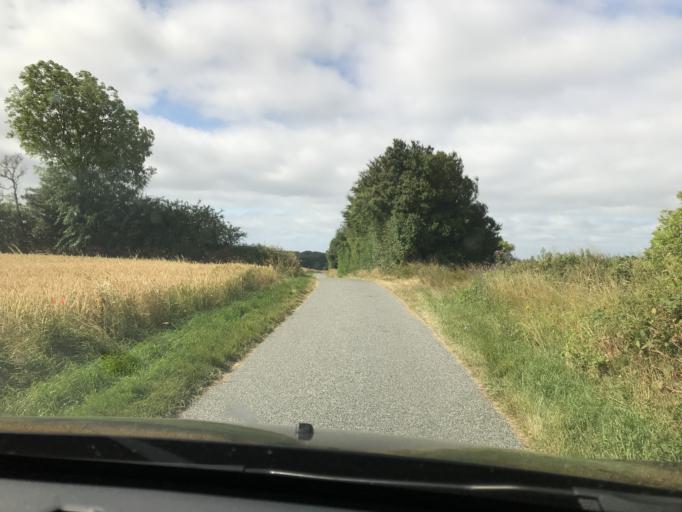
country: DK
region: South Denmark
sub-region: AEro Kommune
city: AEroskobing
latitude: 54.9242
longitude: 10.2894
